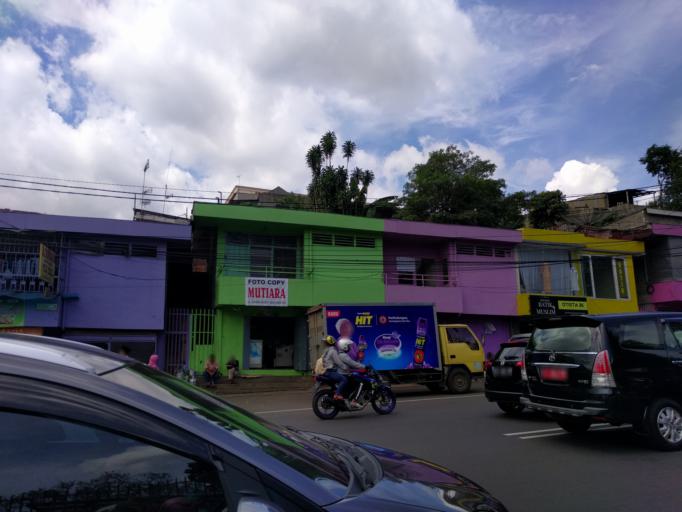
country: ID
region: West Java
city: Bogor
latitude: -6.6024
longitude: 106.8012
